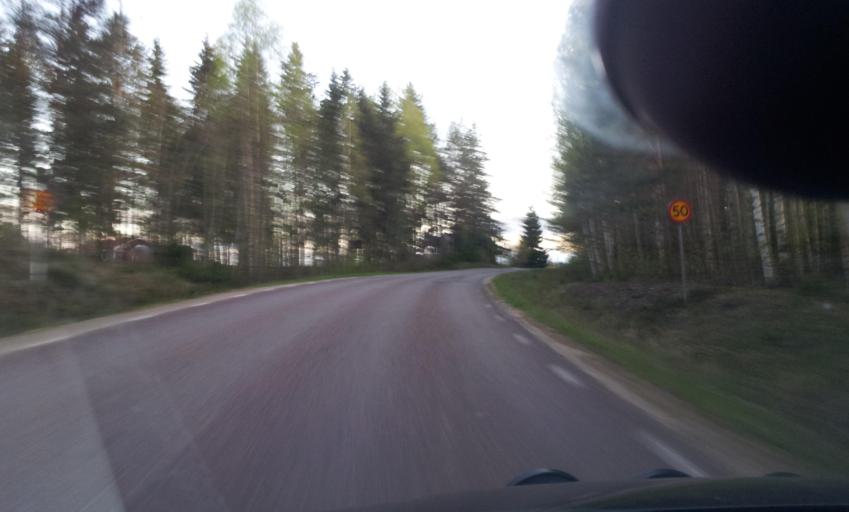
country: SE
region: Gaevleborg
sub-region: Bollnas Kommun
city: Bollnas
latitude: 61.3762
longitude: 16.4033
